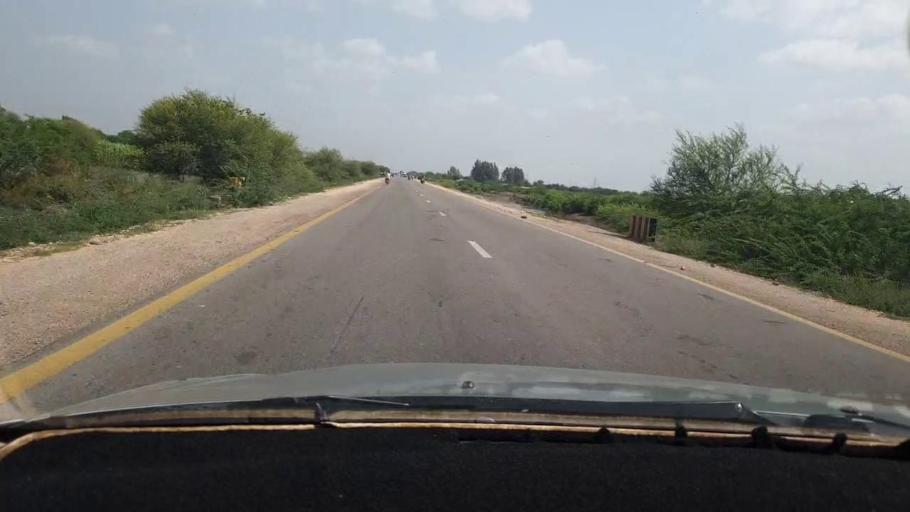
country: PK
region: Sindh
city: Digri
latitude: 25.1120
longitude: 69.1600
